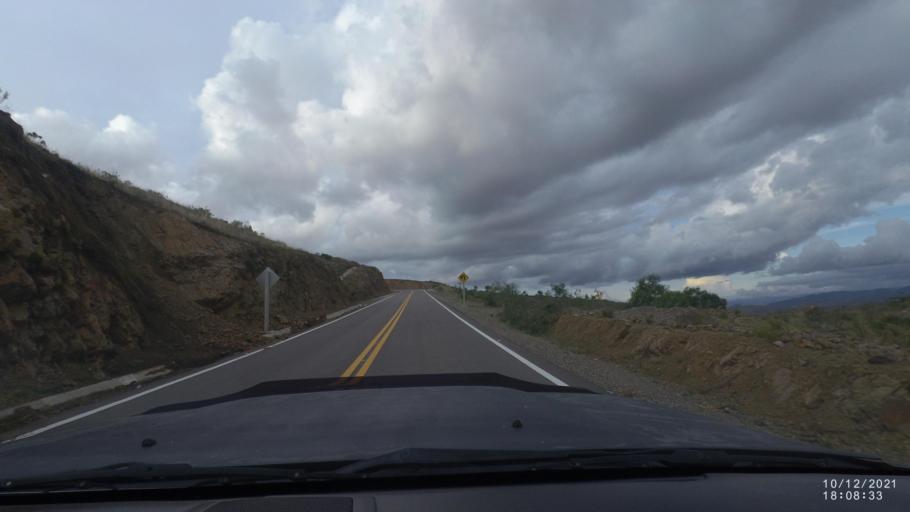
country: BO
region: Cochabamba
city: Tarata
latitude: -17.7917
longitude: -65.9463
